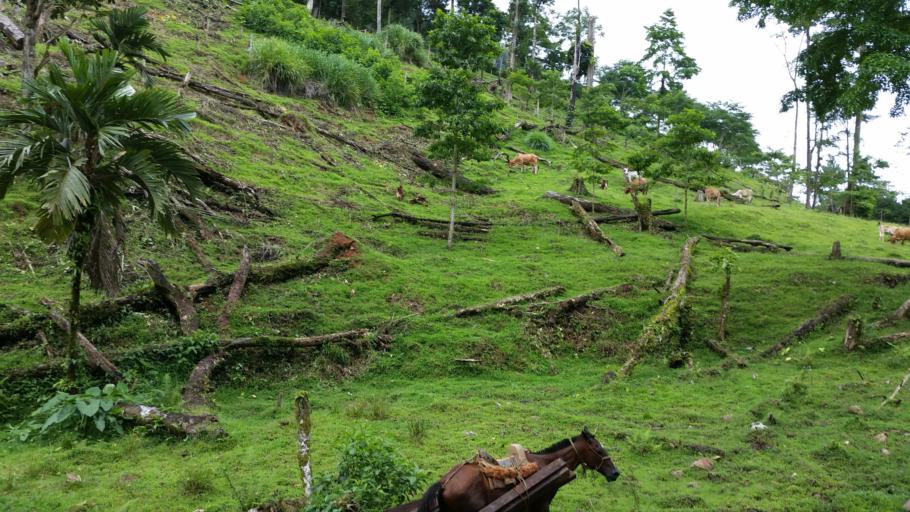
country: NI
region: Atlantico Norte (RAAN)
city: Bonanza
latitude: 13.9921
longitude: -84.7538
